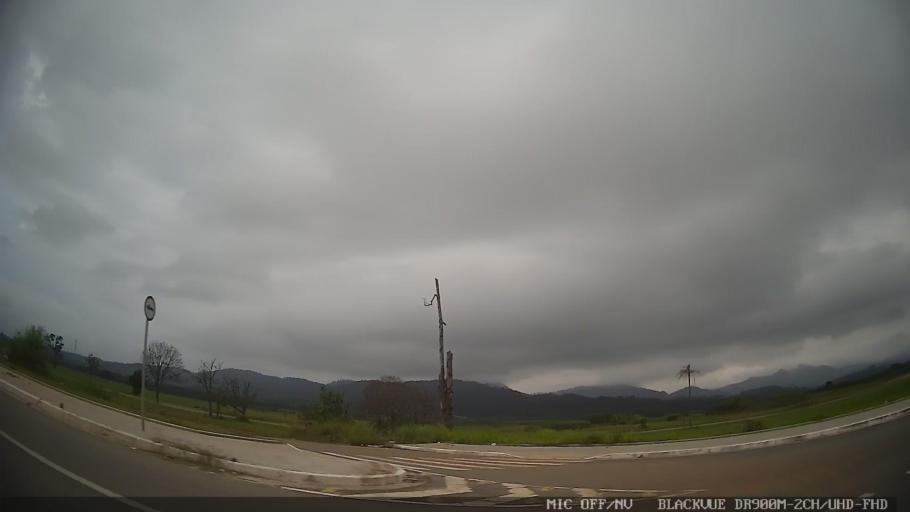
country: BR
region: Sao Paulo
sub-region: Mogi das Cruzes
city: Mogi das Cruzes
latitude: -23.5367
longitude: -46.2337
